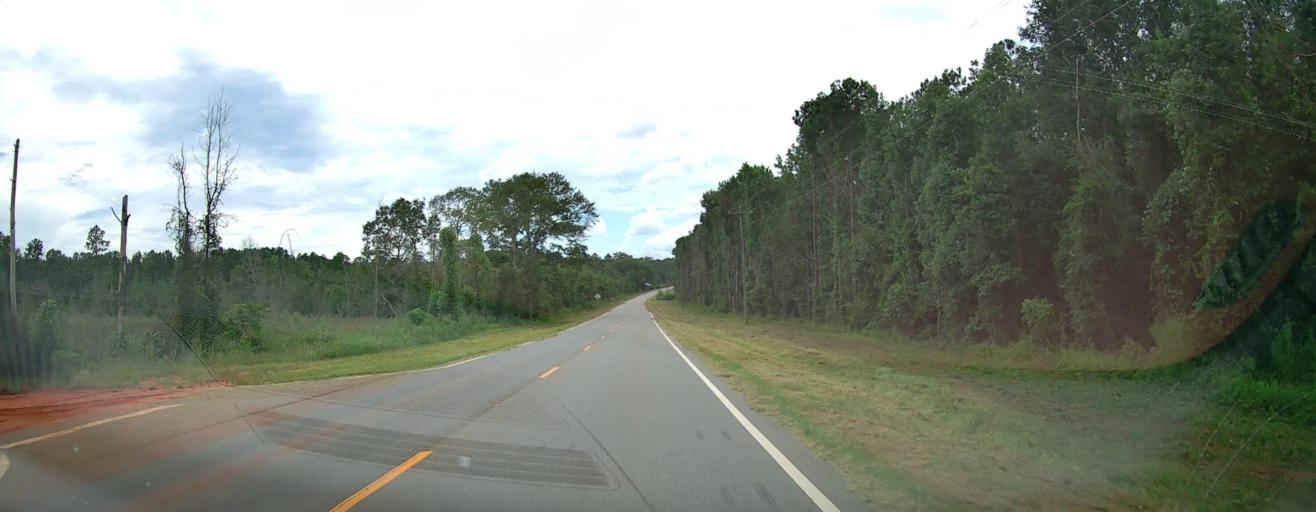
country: US
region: Georgia
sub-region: Schley County
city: Ellaville
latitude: 32.2644
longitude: -84.1942
